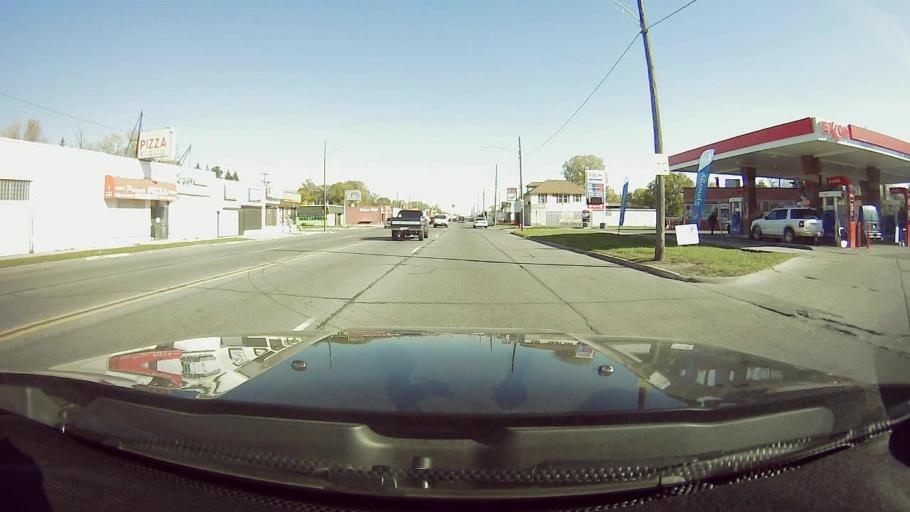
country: US
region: Michigan
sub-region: Oakland County
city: Oak Park
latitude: 42.4302
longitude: -83.2113
